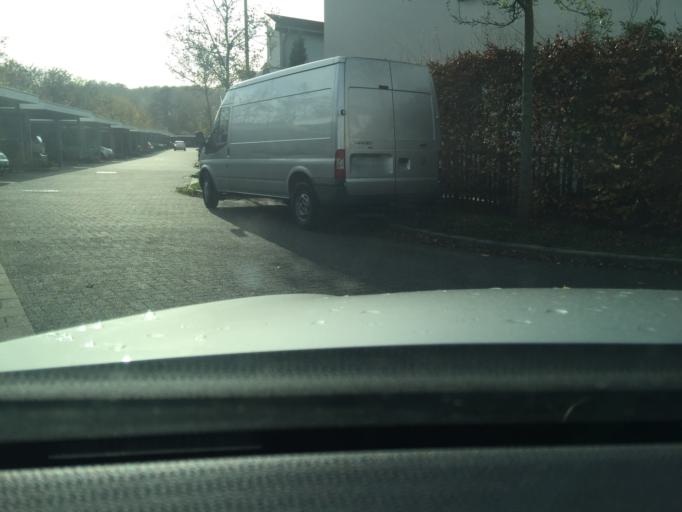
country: DE
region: North Rhine-Westphalia
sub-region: Regierungsbezirk Dusseldorf
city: Velbert
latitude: 51.3850
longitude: 7.0783
